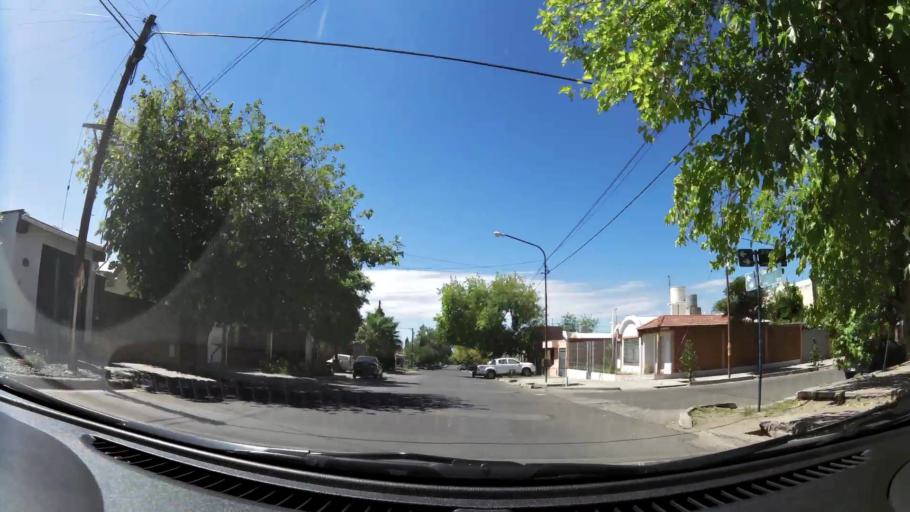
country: AR
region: Mendoza
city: Las Heras
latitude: -32.8378
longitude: -68.8693
